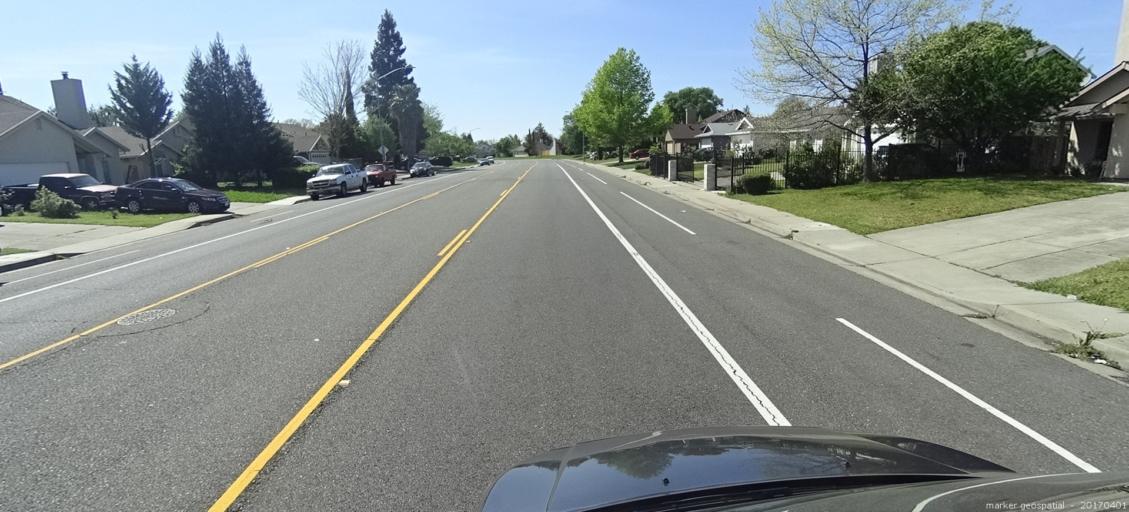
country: US
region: California
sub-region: Sacramento County
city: Laguna
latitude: 38.4511
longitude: -121.4349
